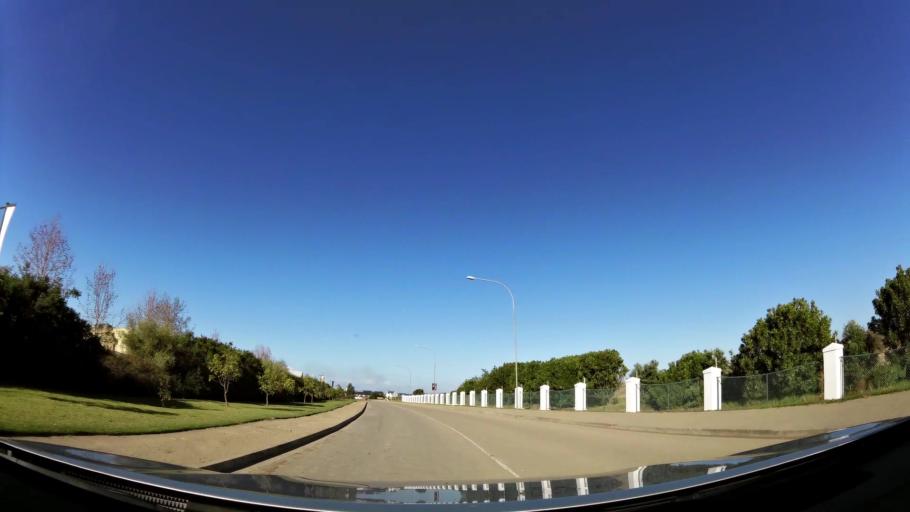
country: ZA
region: Western Cape
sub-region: Eden District Municipality
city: George
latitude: -33.9669
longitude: 22.4293
